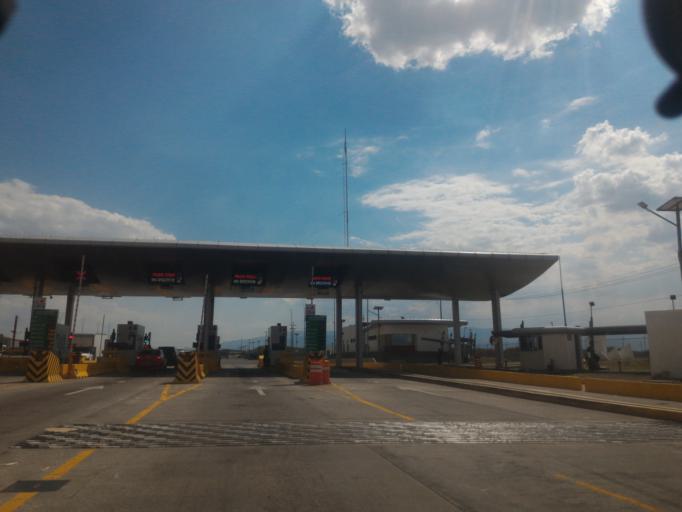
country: MX
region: Jalisco
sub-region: Acatlan de Juarez
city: Villa de los Ninos
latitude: 20.3739
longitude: -103.5764
